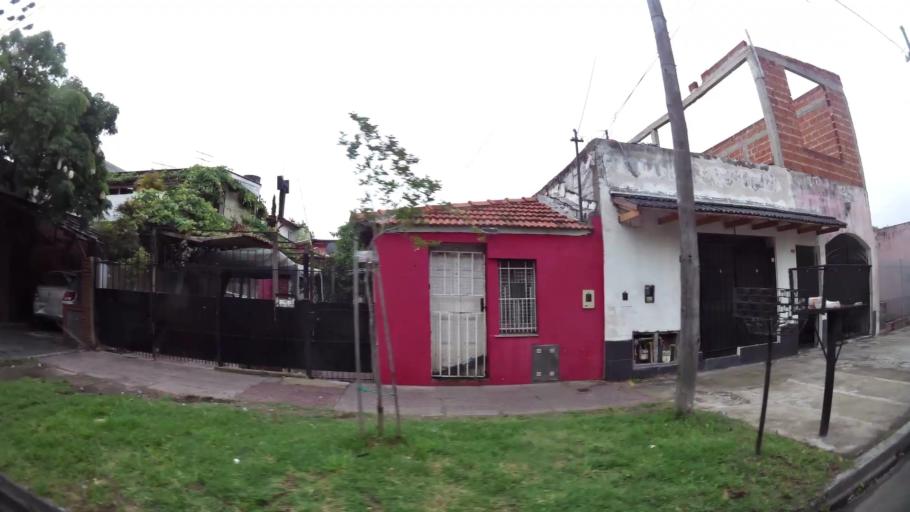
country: AR
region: Buenos Aires
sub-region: Partido de Lanus
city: Lanus
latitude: -34.7124
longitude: -58.3548
